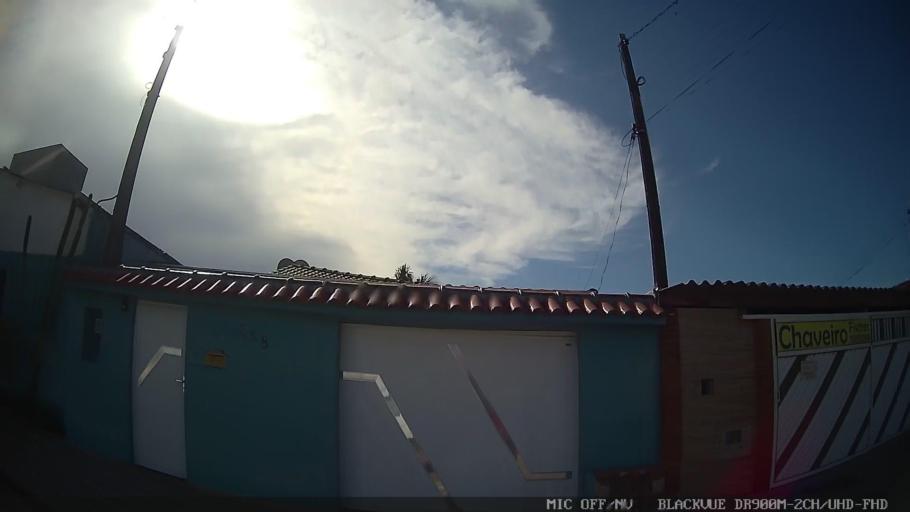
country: BR
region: Sao Paulo
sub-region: Iguape
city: Iguape
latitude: -24.7049
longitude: -47.5620
